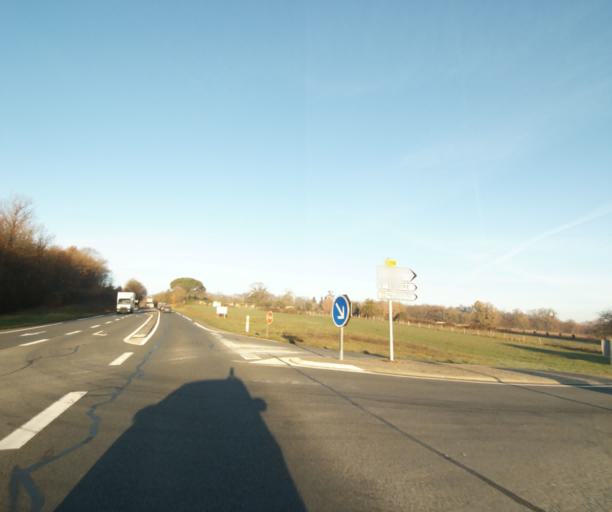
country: FR
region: Poitou-Charentes
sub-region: Departement de la Charente-Maritime
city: Chaniers
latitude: 45.7398
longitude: -0.5434
